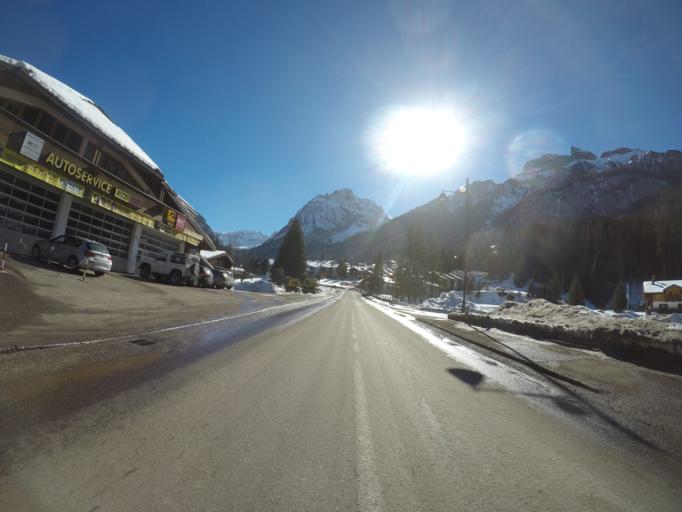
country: IT
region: Trentino-Alto Adige
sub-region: Provincia di Trento
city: Canazei
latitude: 46.4697
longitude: 11.7786
